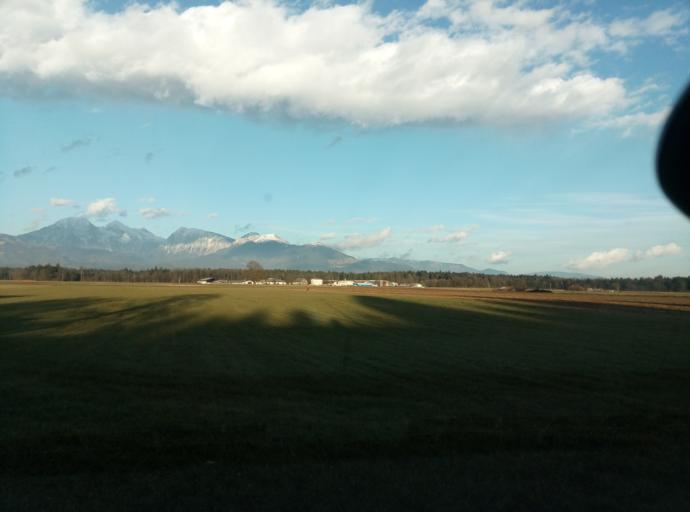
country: SI
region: Sencur
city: Hrastje
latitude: 46.2203
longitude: 14.3833
